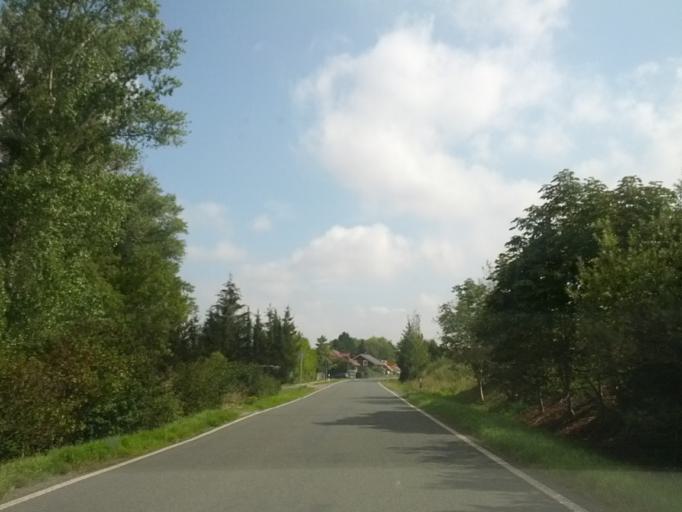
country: DE
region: Thuringia
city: Wandersleben
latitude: 50.8998
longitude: 10.8419
